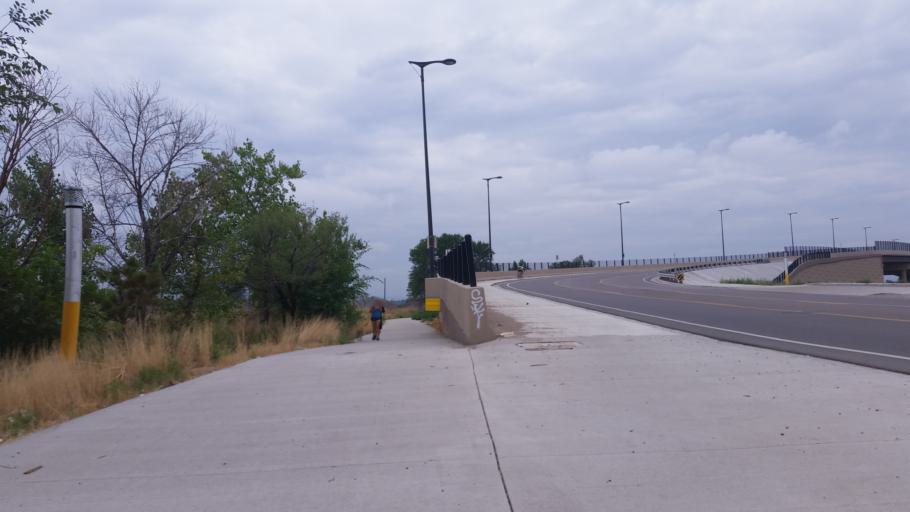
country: US
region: Colorado
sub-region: Adams County
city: Twin Lakes
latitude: 39.8133
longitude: -105.0105
